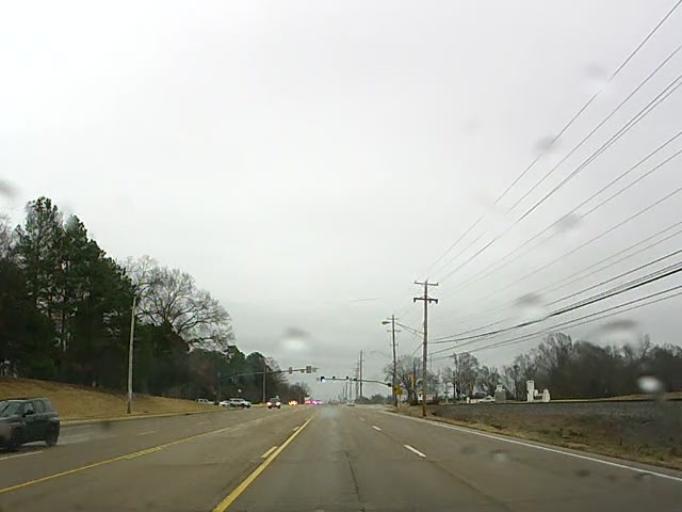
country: US
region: Tennessee
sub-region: Shelby County
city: Collierville
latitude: 35.0473
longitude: -89.7130
